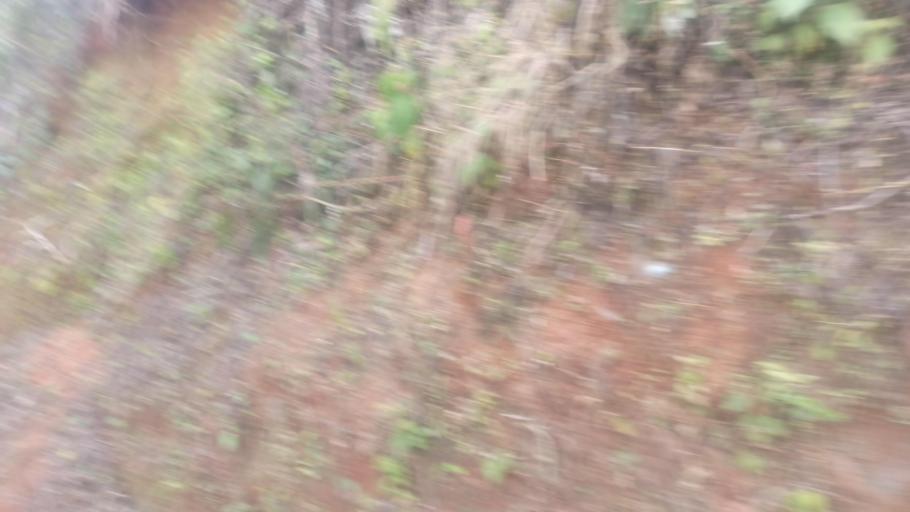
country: CO
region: Valle del Cauca
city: Jamundi
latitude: 3.1858
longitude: -76.6761
